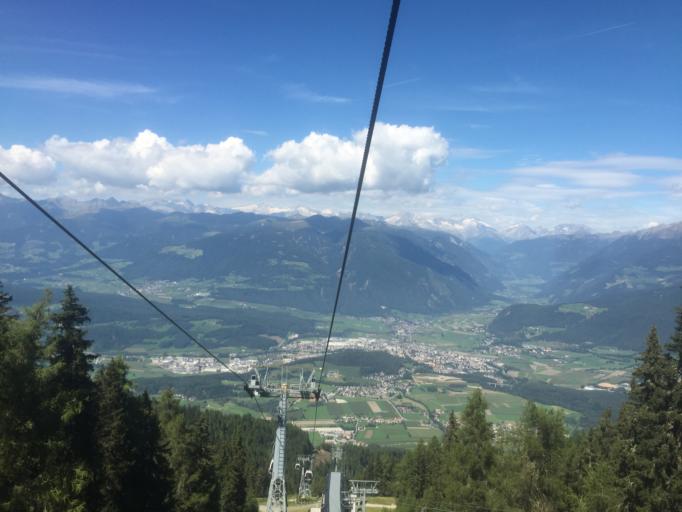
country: IT
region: Trentino-Alto Adige
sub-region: Bolzano
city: Riscone
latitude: 46.7468
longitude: 11.9534
